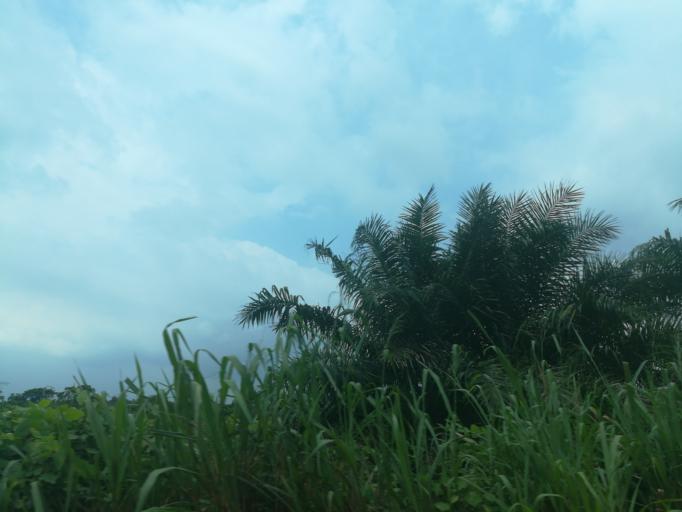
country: NG
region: Lagos
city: Ikorodu
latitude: 6.6733
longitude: 3.6573
